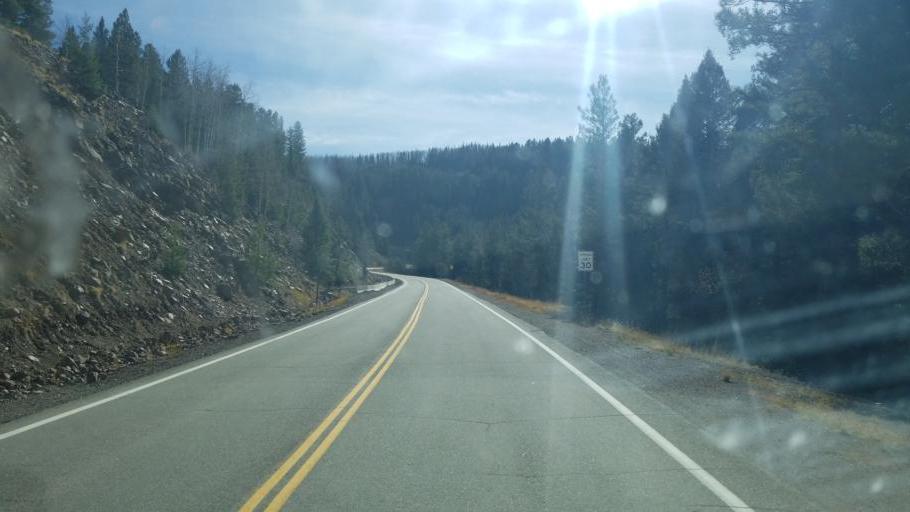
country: US
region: New Mexico
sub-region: Rio Arriba County
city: Chama
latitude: 37.1146
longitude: -106.3741
